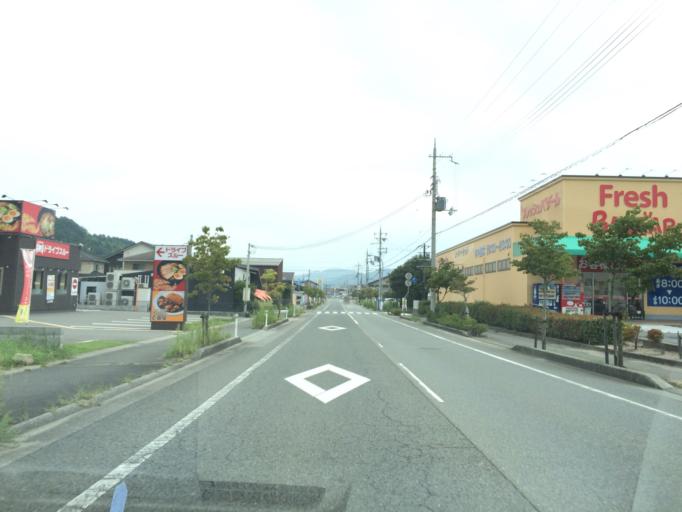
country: JP
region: Hyogo
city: Toyooka
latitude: 35.5388
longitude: 134.8091
